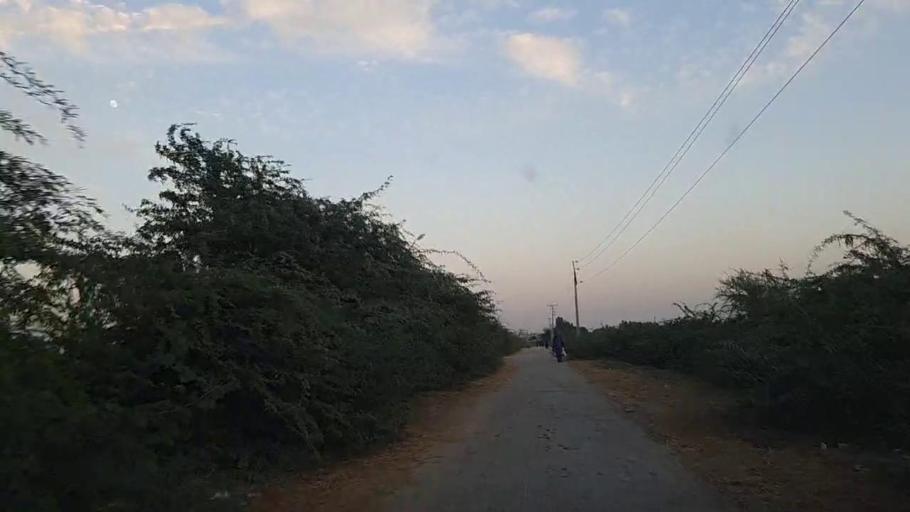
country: PK
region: Sindh
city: Thatta
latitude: 24.7956
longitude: 67.9547
